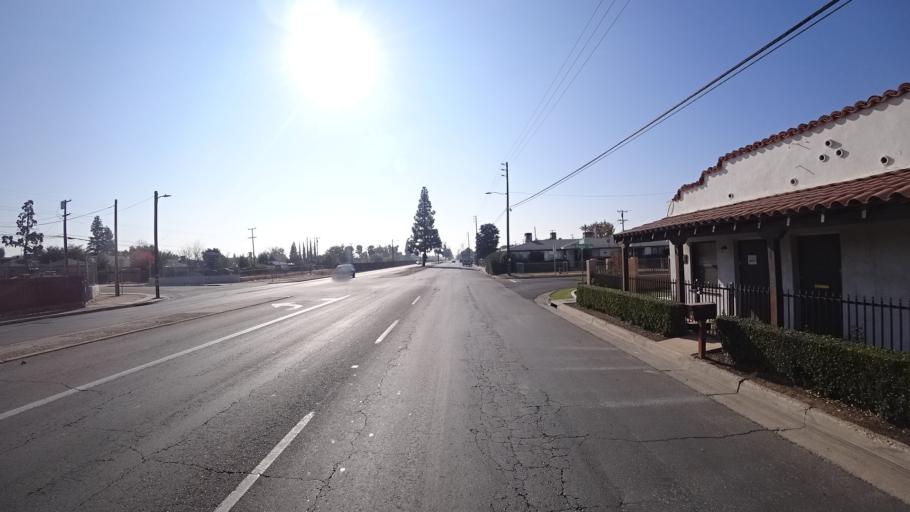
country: US
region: California
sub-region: Kern County
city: Bakersfield
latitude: 35.3432
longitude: -119.0212
